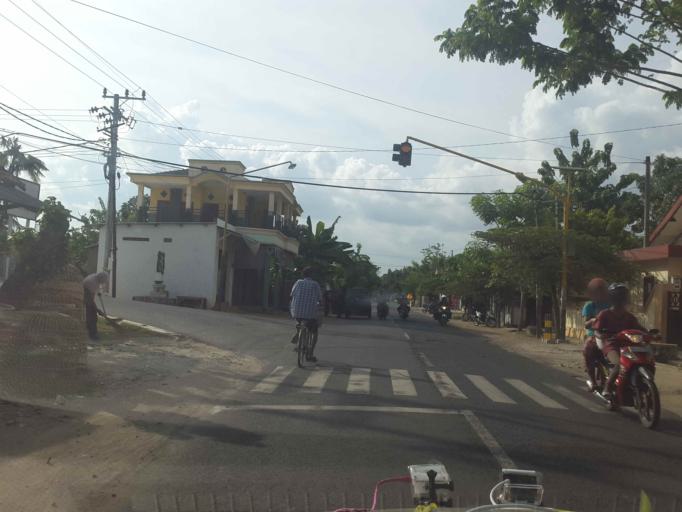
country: ID
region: East Java
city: Masjid
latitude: -7.0374
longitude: 113.8969
